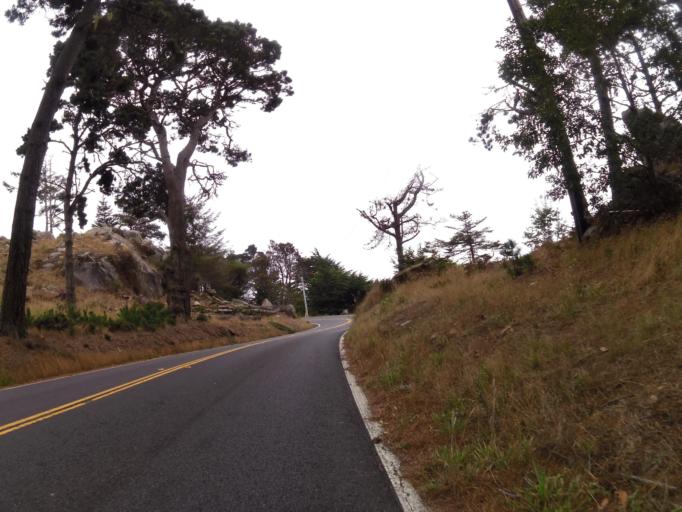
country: US
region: California
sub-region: Sonoma County
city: Sea Ranch
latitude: 38.5431
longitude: -123.2918
